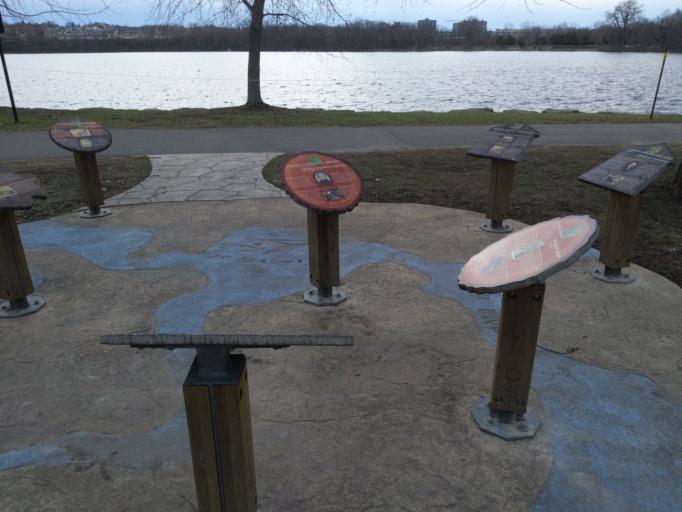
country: CA
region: Quebec
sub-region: Outaouais
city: Gatineau
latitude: 45.4522
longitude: -75.7195
